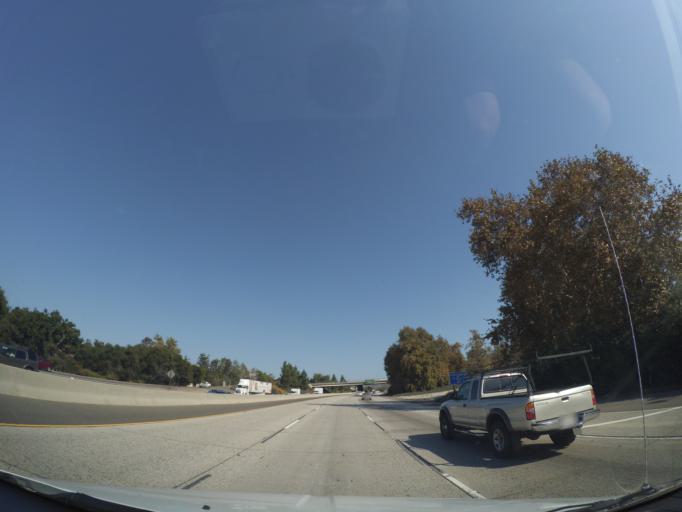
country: US
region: California
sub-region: Ventura County
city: Casa Conejo
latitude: 34.1828
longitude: -118.8905
